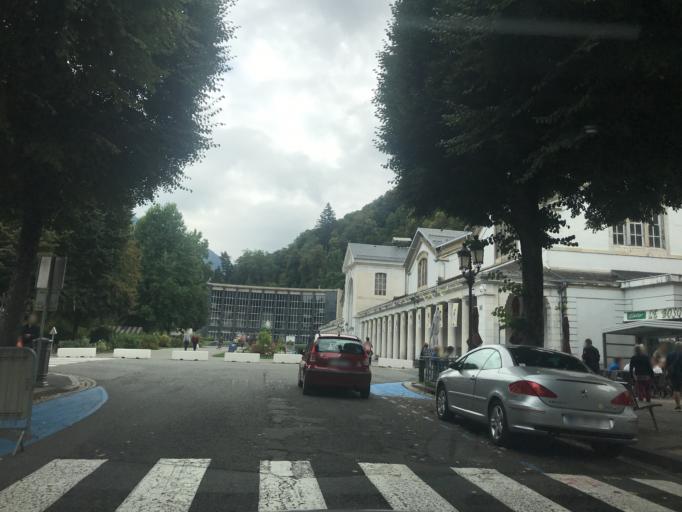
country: FR
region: Midi-Pyrenees
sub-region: Departement de la Haute-Garonne
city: Bagneres-de-Luchon
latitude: 42.7860
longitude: 0.5938
